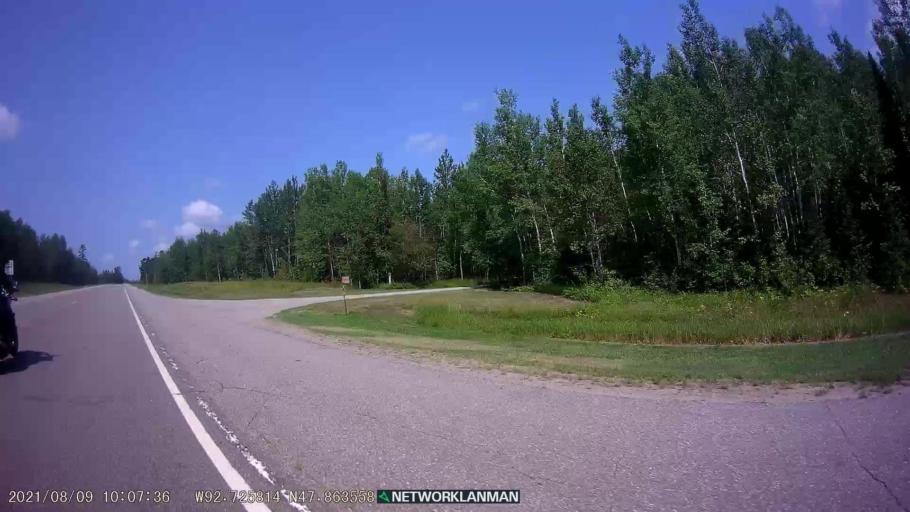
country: US
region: Minnesota
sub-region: Saint Louis County
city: Mountain Iron
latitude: 47.8635
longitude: -92.7254
